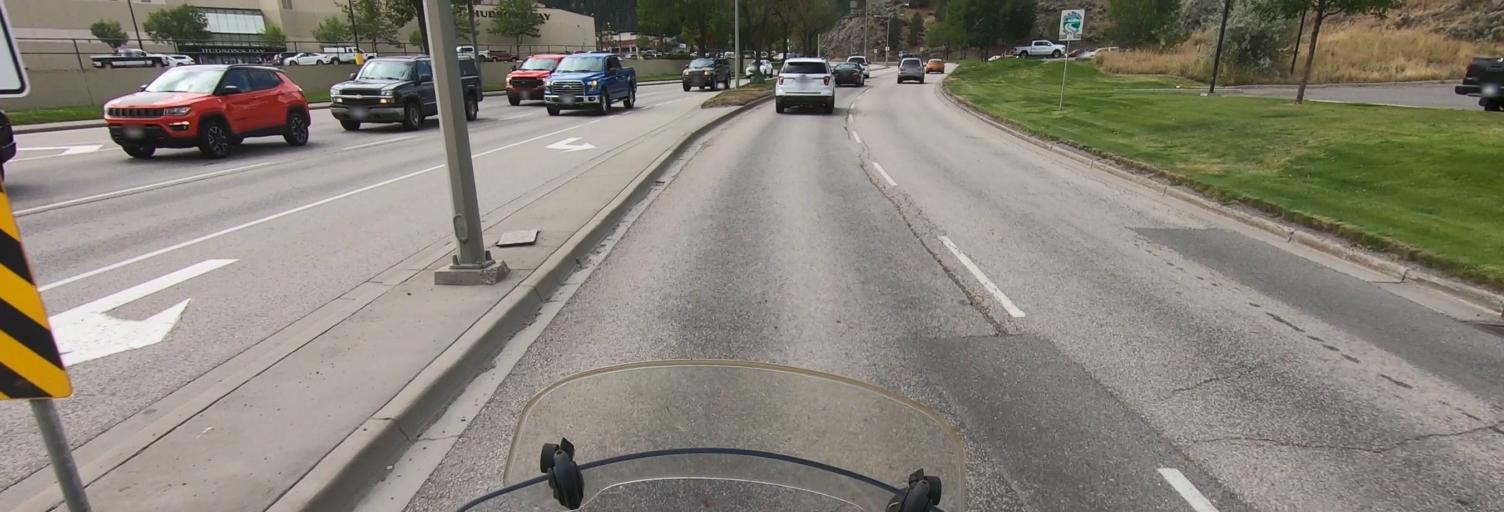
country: CA
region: British Columbia
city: Kamloops
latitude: 50.6574
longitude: -120.3705
